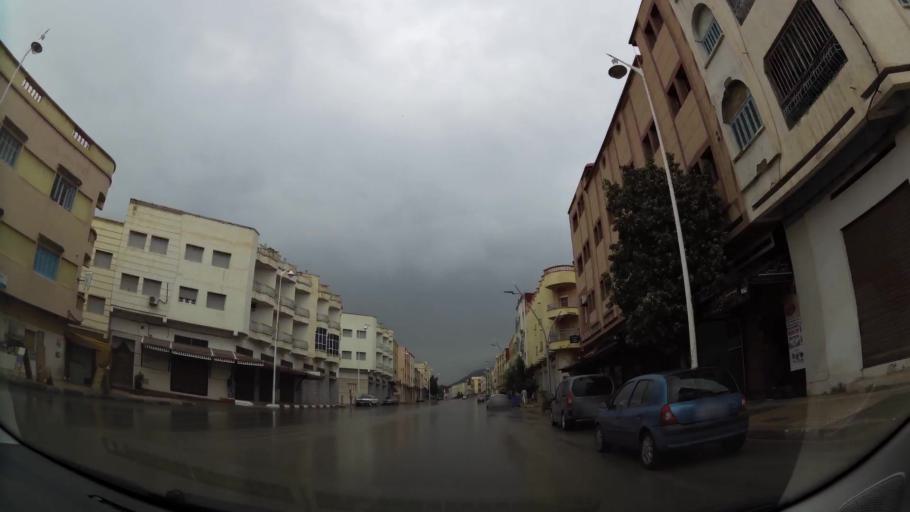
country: MA
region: Oriental
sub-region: Nador
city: Nador
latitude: 35.1539
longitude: -2.9885
